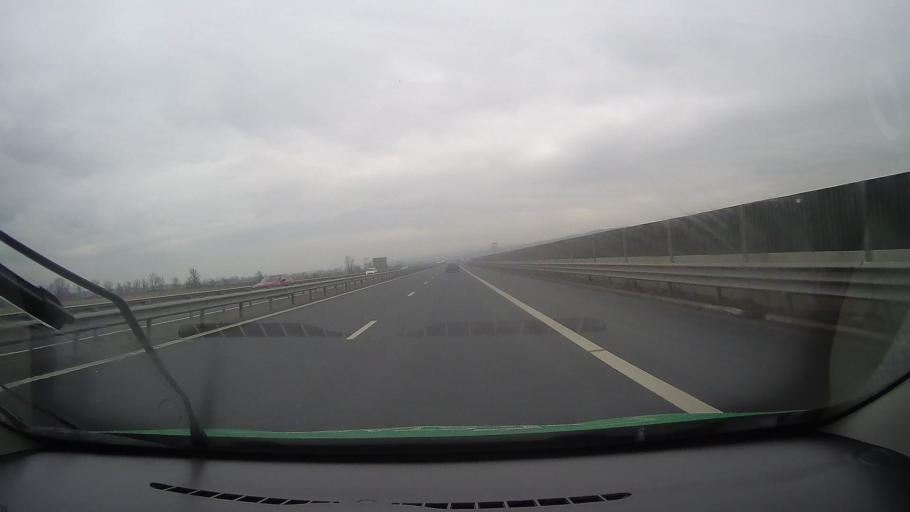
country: RO
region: Hunedoara
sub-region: Comuna Rapoltu Mare
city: Rapoltu Mare
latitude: 45.8468
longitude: 23.0588
